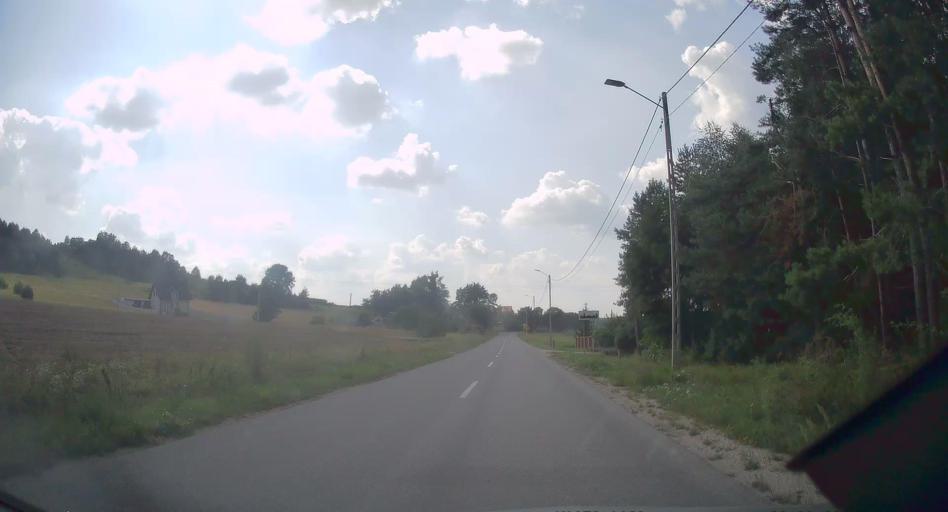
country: PL
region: Swietokrzyskie
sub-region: Powiat jedrzejowski
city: Malogoszcz
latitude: 50.8637
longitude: 20.3310
